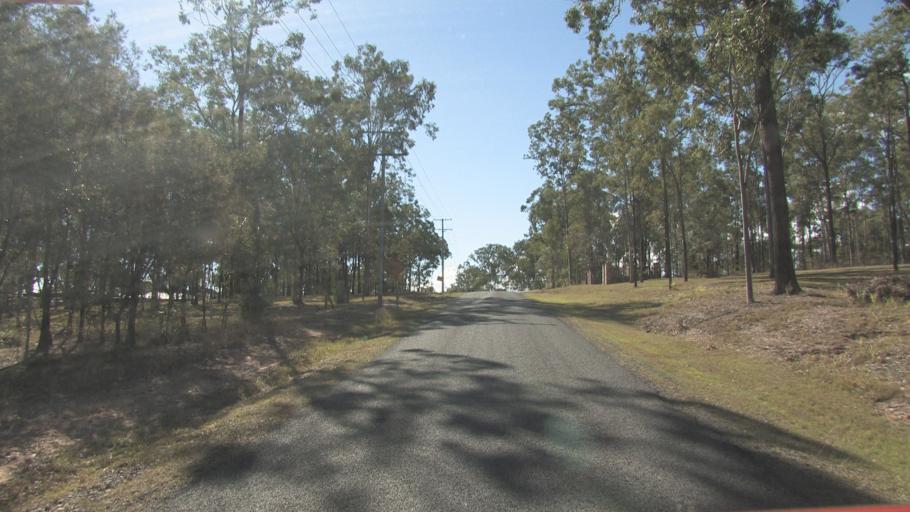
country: AU
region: Queensland
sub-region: Logan
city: Chambers Flat
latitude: -27.8084
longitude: 153.0788
